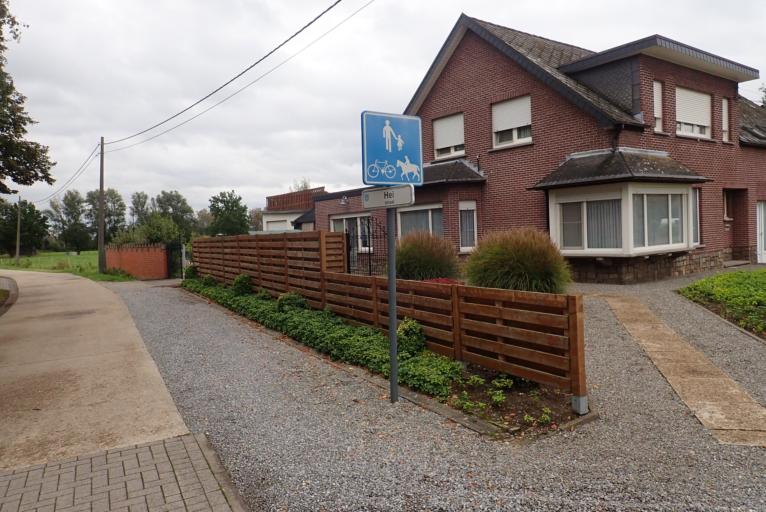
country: BE
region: Flanders
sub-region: Provincie Antwerpen
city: Heist-op-den-Berg
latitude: 51.0642
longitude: 4.7450
